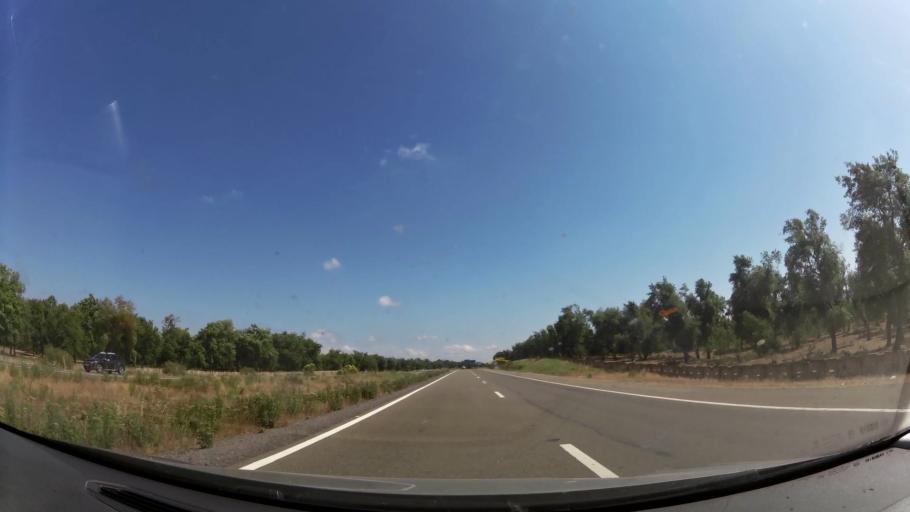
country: MA
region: Rabat-Sale-Zemmour-Zaer
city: Sale
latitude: 34.1079
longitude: -6.6862
